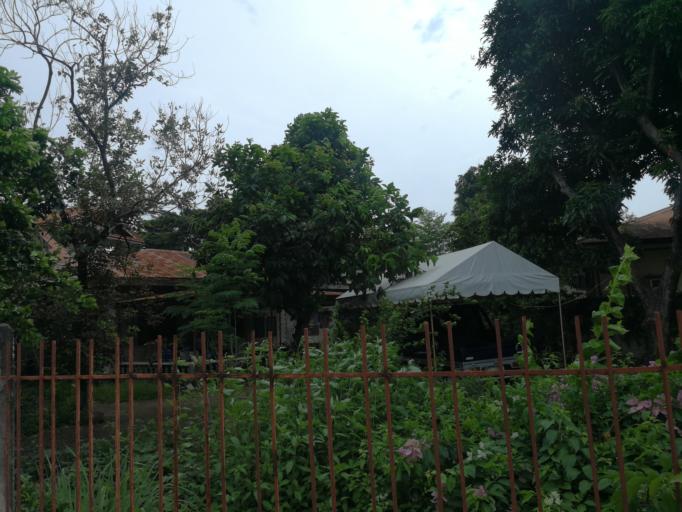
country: PH
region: Central Visayas
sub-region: Province of Negros Oriental
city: Dumaguete
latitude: 9.3033
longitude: 123.2990
